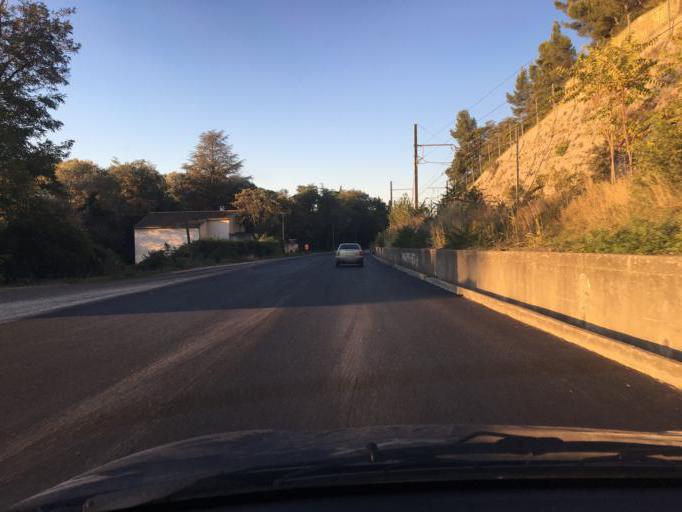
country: FR
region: Languedoc-Roussillon
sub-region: Departement du Gard
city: Villeneuve-les-Avignon
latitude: 43.9821
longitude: 4.8051
